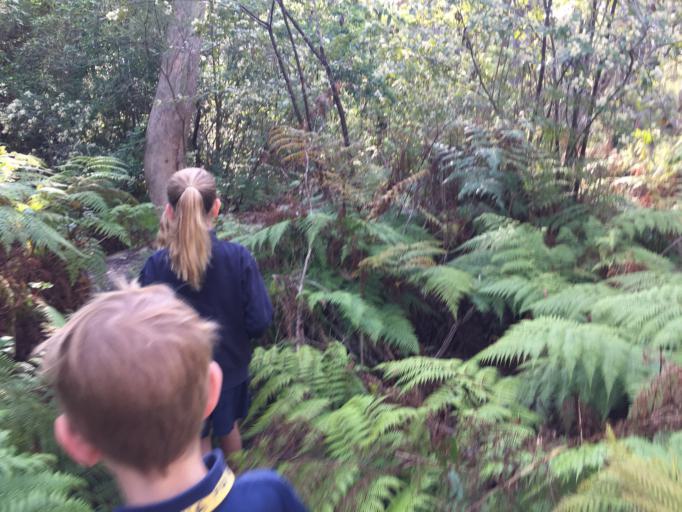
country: AU
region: New South Wales
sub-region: Ryde
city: East Ryde
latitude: -33.8127
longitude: 151.1327
